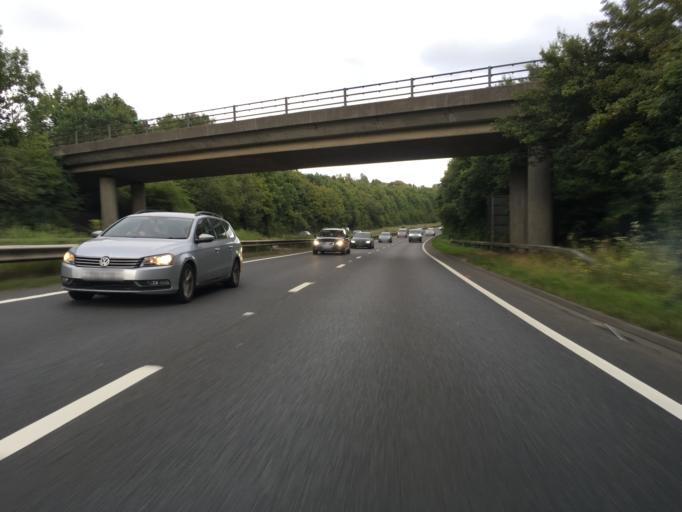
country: GB
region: England
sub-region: Hampshire
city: Petersfield
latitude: 51.0156
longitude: -0.9468
